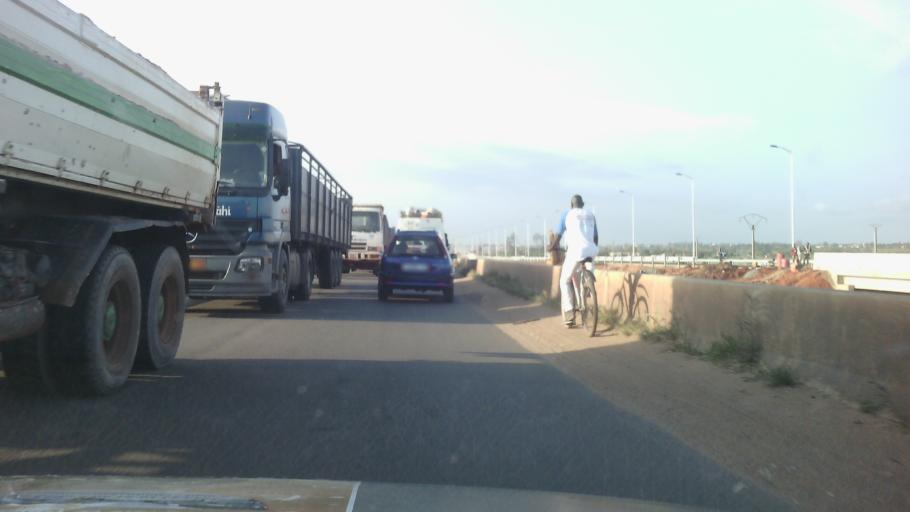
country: TG
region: Maritime
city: Tsevie
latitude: 6.2881
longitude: 1.2127
